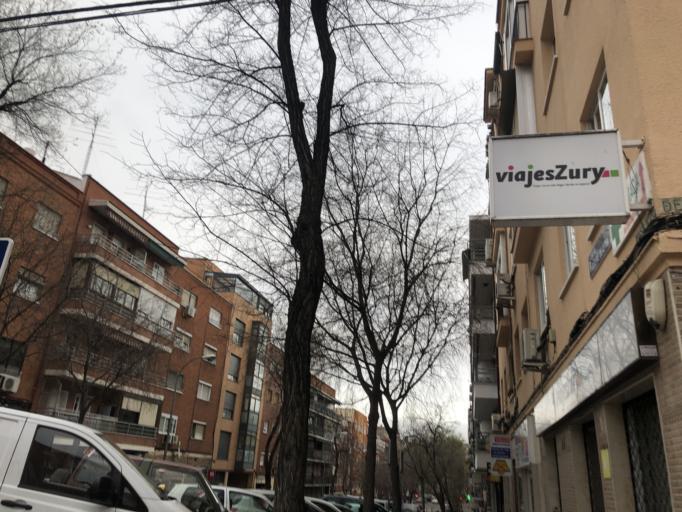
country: ES
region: Madrid
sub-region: Provincia de Madrid
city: Moratalaz
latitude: 40.4333
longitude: -3.6437
